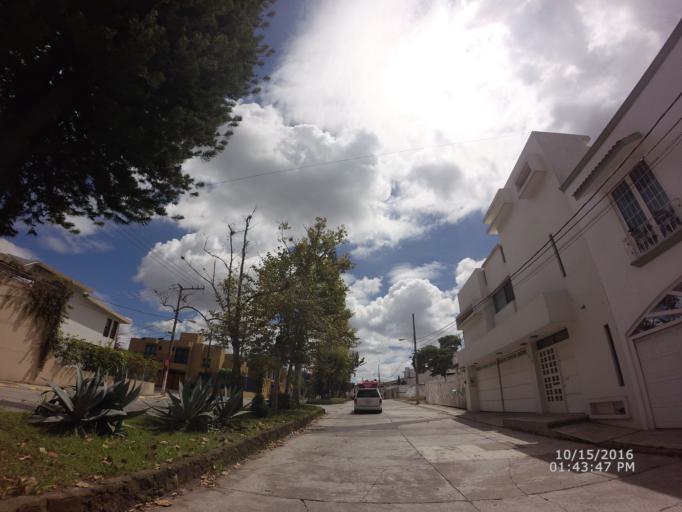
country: MX
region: Veracruz
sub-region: Xalapa
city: Lomas Verdes
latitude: 19.5287
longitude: -96.8868
